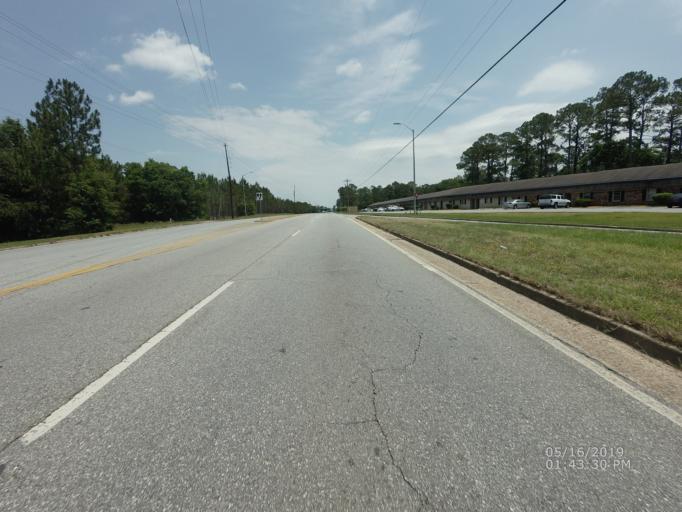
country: US
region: Georgia
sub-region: Dougherty County
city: Albany
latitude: 31.5489
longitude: -84.1979
